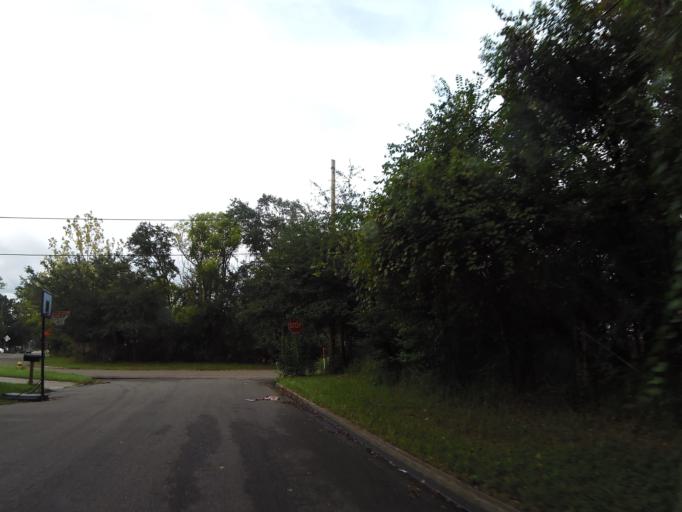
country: US
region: Florida
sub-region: Duval County
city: Jacksonville
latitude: 30.3515
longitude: -81.7059
